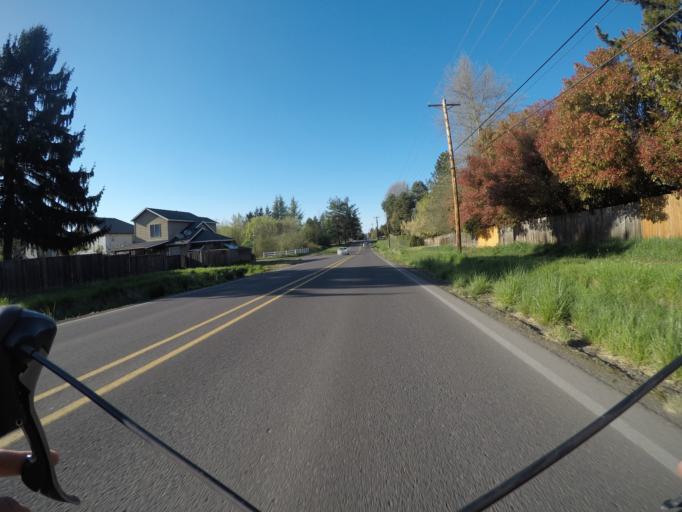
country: US
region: Oregon
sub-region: Washington County
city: Aloha
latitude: 45.4690
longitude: -122.8675
